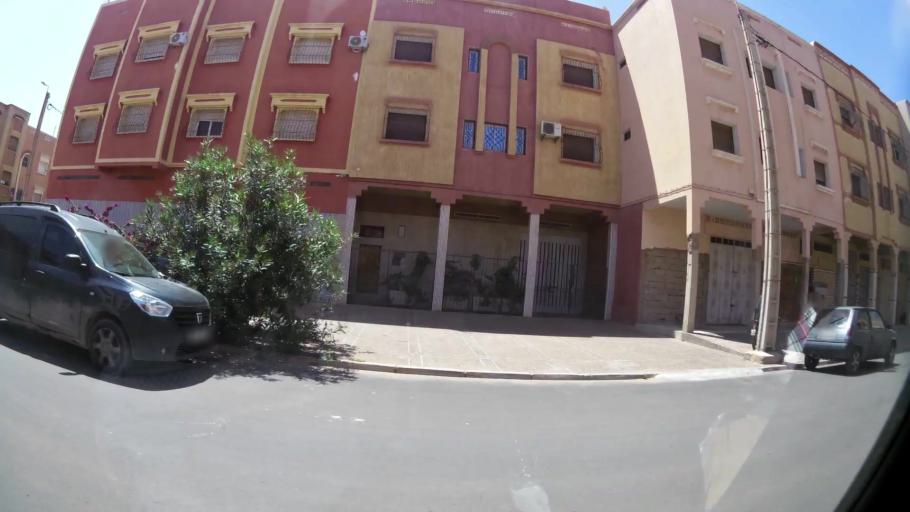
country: MA
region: Souss-Massa-Draa
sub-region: Inezgane-Ait Mellou
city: Inezgane
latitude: 30.3481
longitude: -9.4840
